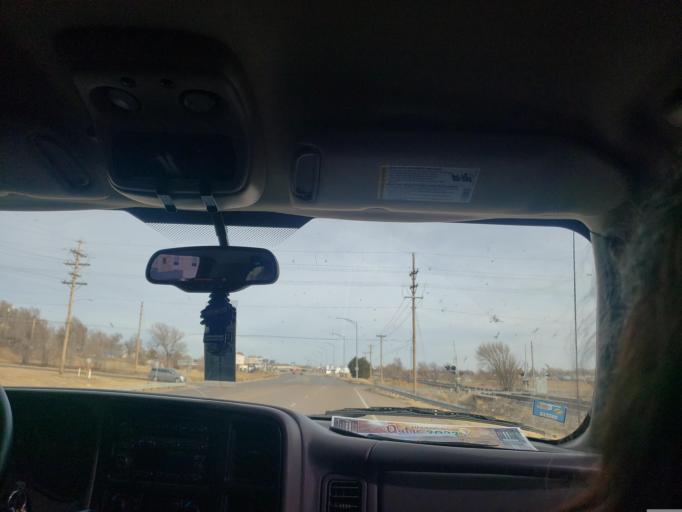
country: US
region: Kansas
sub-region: Ford County
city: Dodge City
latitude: 37.7543
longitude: -100.0522
